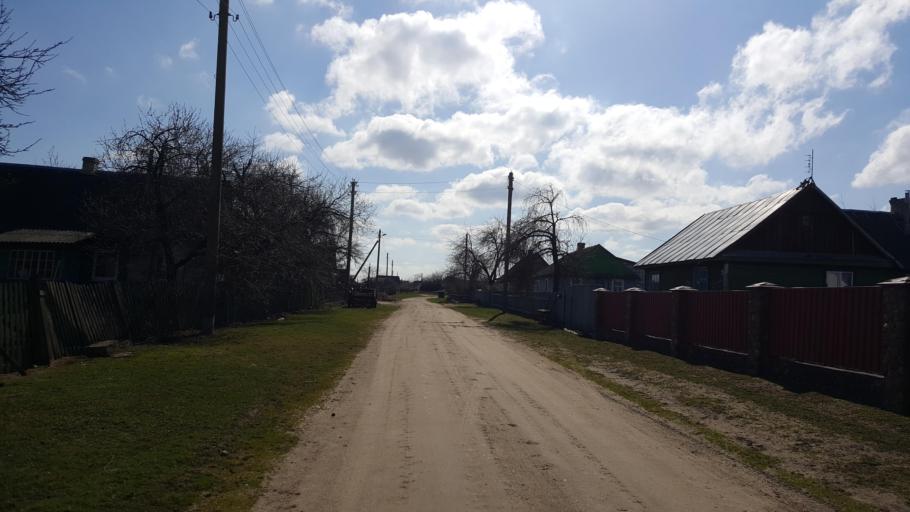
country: BY
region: Brest
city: Kamyanyets
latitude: 52.4069
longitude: 23.8000
